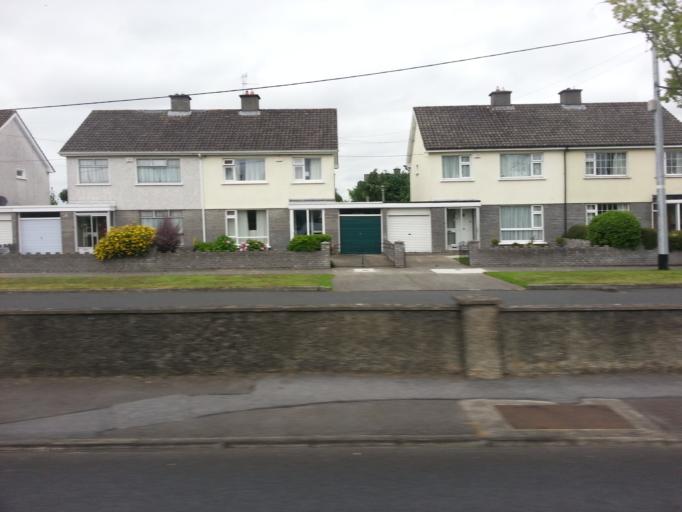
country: IE
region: Leinster
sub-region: Kilkenny
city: Kilkenny
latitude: 52.6504
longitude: -7.2328
